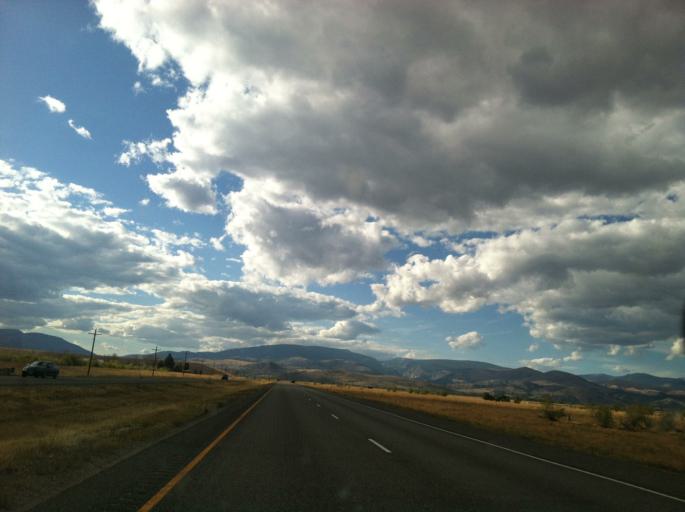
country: US
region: Montana
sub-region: Deer Lodge County
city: Anaconda
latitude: 46.1095
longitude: -112.8537
